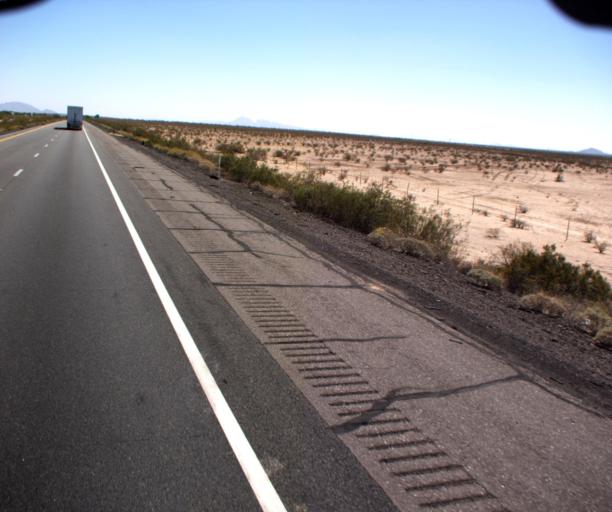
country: US
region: Arizona
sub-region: La Paz County
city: Salome
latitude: 33.5727
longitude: -113.3792
